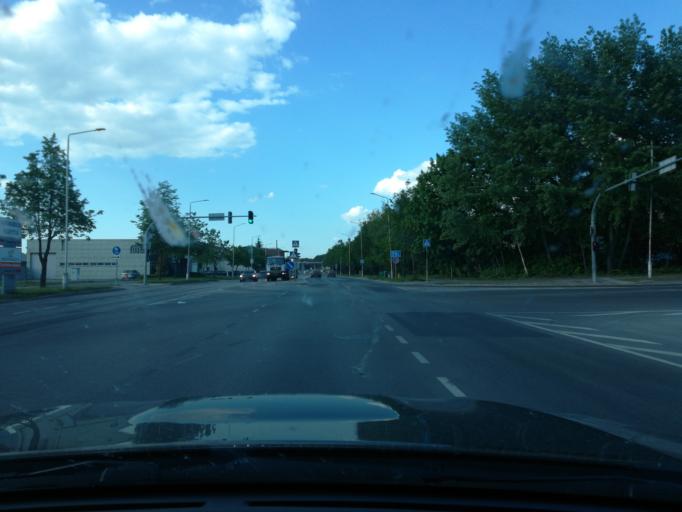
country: LT
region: Kauno apskritis
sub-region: Kaunas
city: Eiguliai
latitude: 54.9306
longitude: 23.9168
